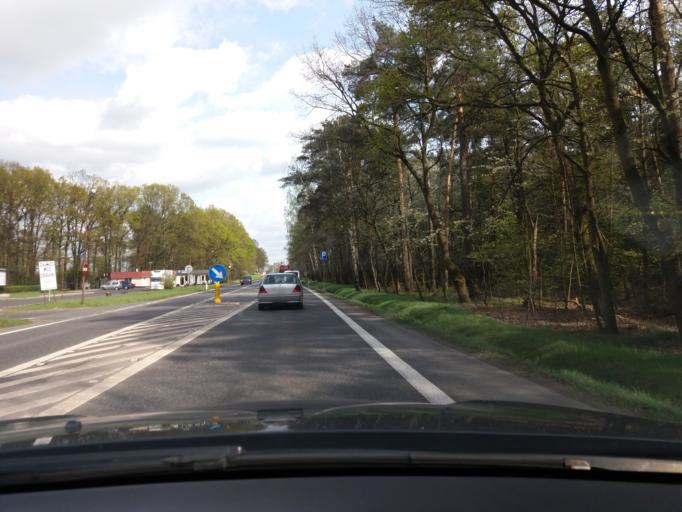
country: PL
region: Lower Silesian Voivodeship
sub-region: Powiat sredzki
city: Mrozow
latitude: 51.1583
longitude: 16.7718
